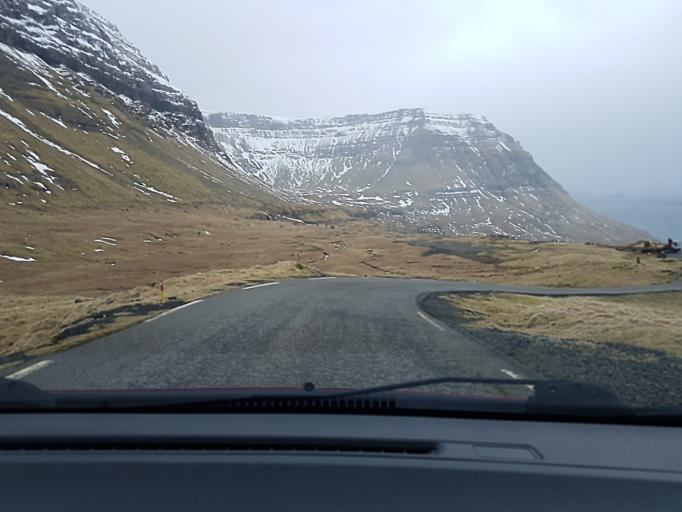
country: FO
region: Streymoy
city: Kollafjordhur
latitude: 62.0521
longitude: -6.9216
